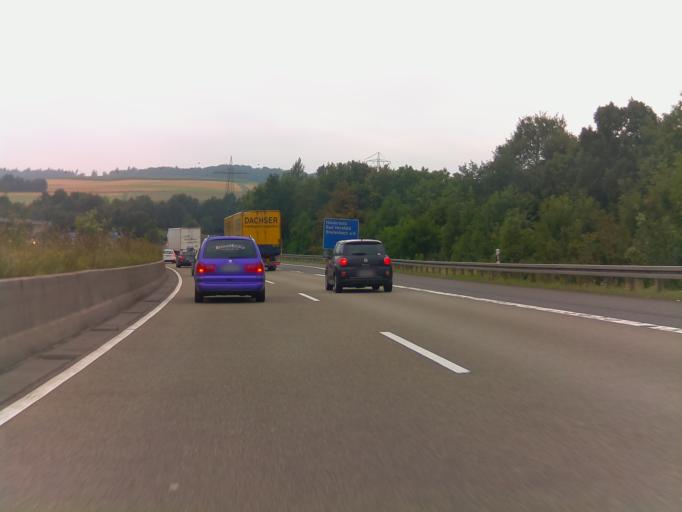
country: DE
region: Hesse
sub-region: Regierungsbezirk Kassel
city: Niederaula
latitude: 50.7740
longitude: 9.5874
